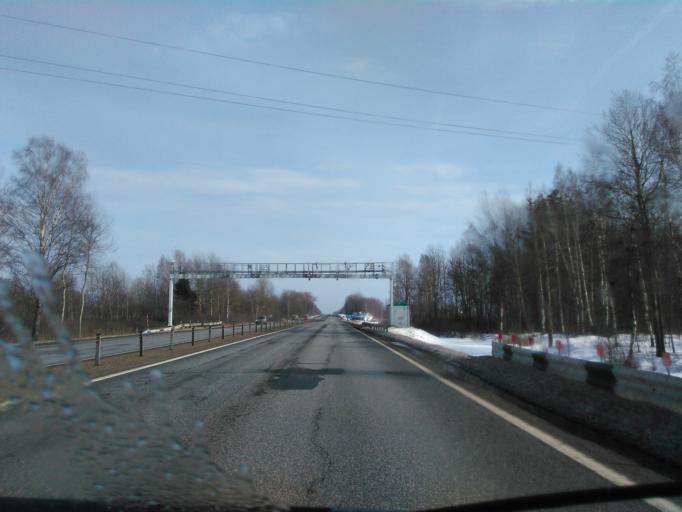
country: BY
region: Vitebsk
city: Dubrowna
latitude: 54.6848
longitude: 30.8082
